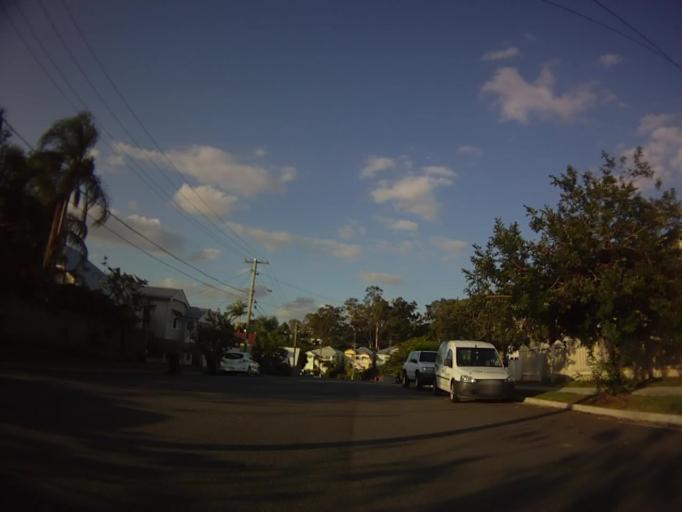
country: AU
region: Queensland
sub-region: Brisbane
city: Milton
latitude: -27.4680
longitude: 153.0009
